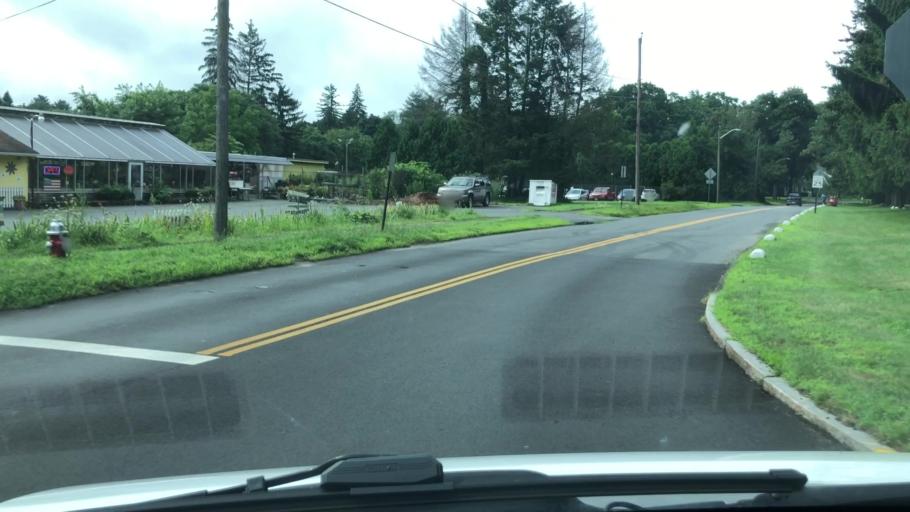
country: US
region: Massachusetts
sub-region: Hampshire County
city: Northampton
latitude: 42.3297
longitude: -72.6452
